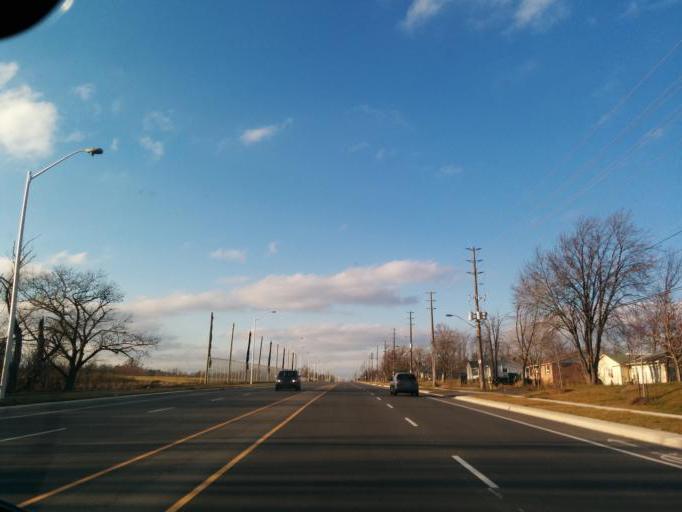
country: CA
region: Ontario
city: Oakville
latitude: 43.4975
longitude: -79.6827
